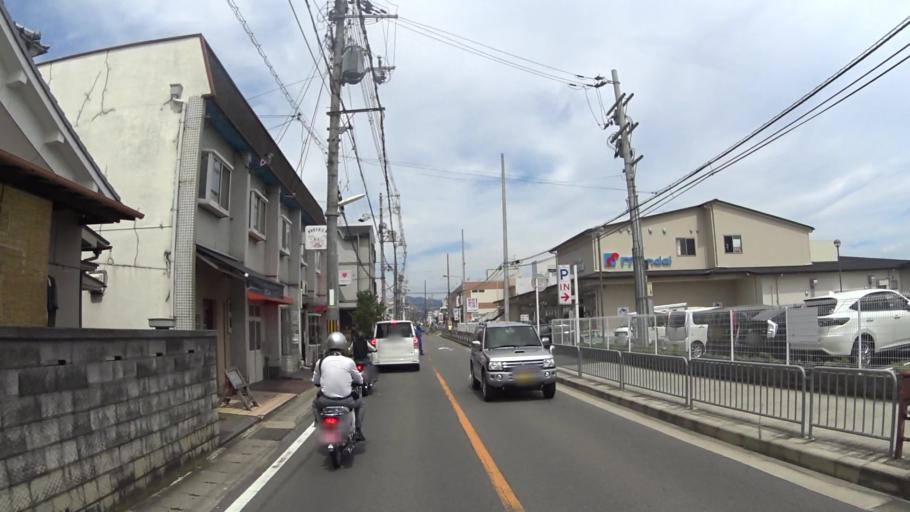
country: JP
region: Kyoto
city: Muko
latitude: 34.9686
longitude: 135.6940
